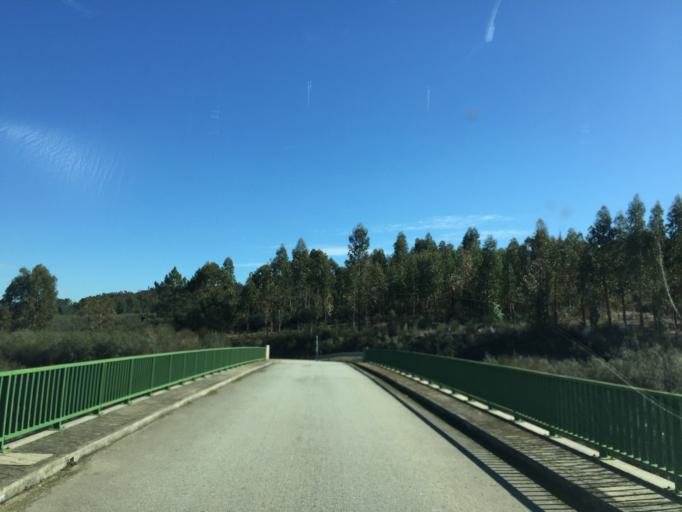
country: PT
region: Portalegre
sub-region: Nisa
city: Nisa
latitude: 39.6206
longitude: -7.7557
